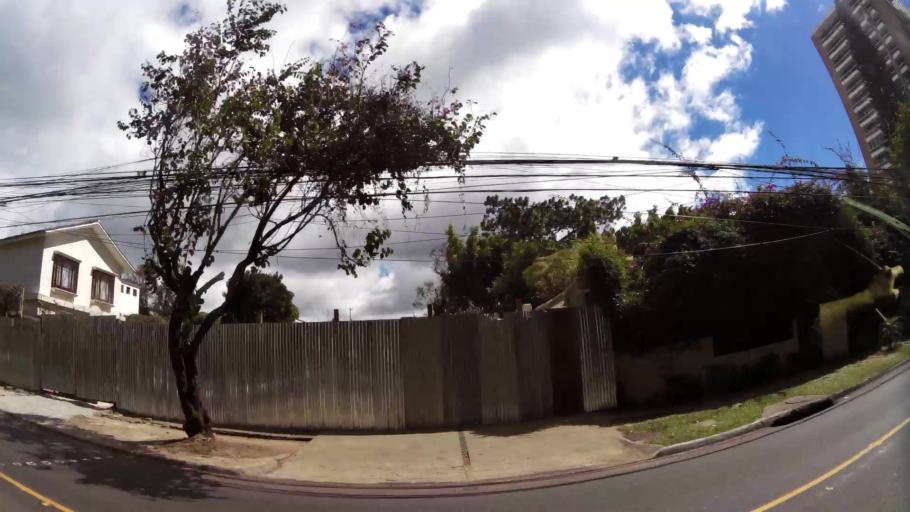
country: GT
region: Guatemala
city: Santa Catarina Pinula
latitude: 14.5810
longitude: -90.5156
